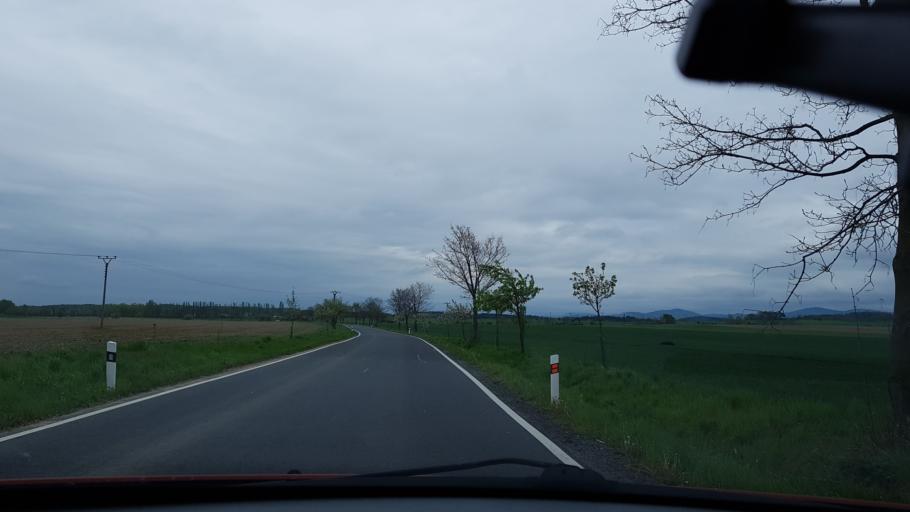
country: CZ
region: Olomoucky
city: Zulova
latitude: 50.3871
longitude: 17.0885
